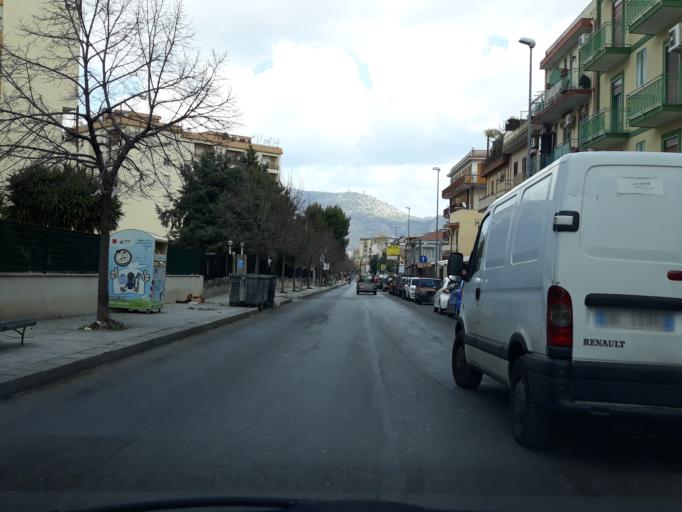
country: IT
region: Sicily
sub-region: Palermo
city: Palermo
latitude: 38.1228
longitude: 13.3093
